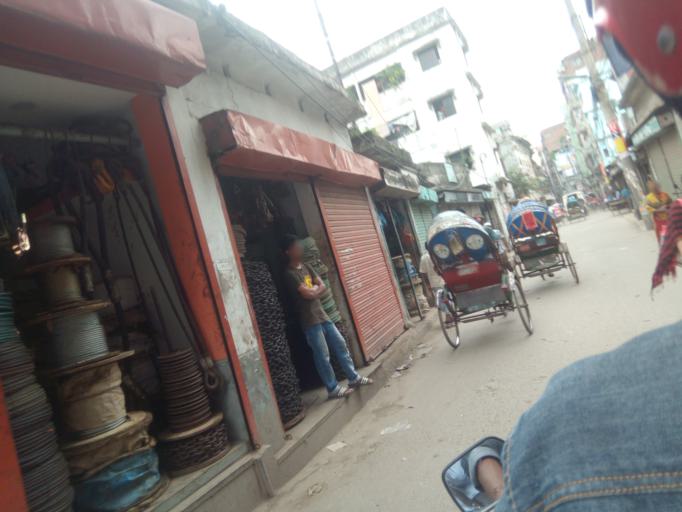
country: BD
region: Dhaka
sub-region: Dhaka
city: Dhaka
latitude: 23.7058
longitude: 90.4180
